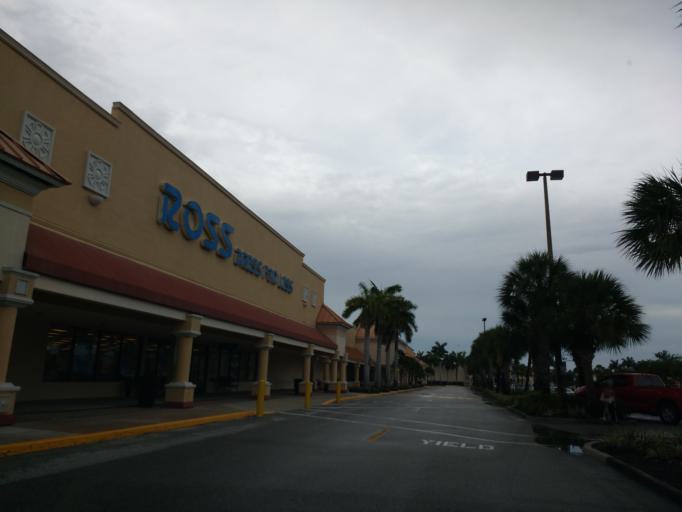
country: US
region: Florida
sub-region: Lee County
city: Villas
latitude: 26.5470
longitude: -81.8750
